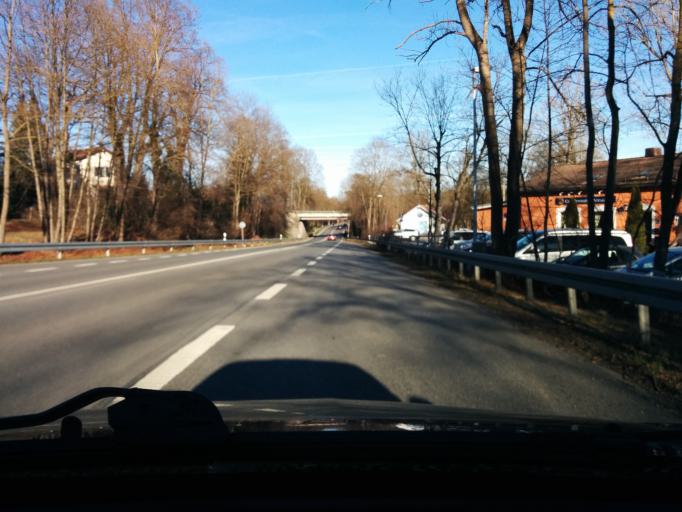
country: DE
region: Bavaria
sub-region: Upper Bavaria
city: Wielenbach
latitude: 47.8564
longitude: 11.1574
